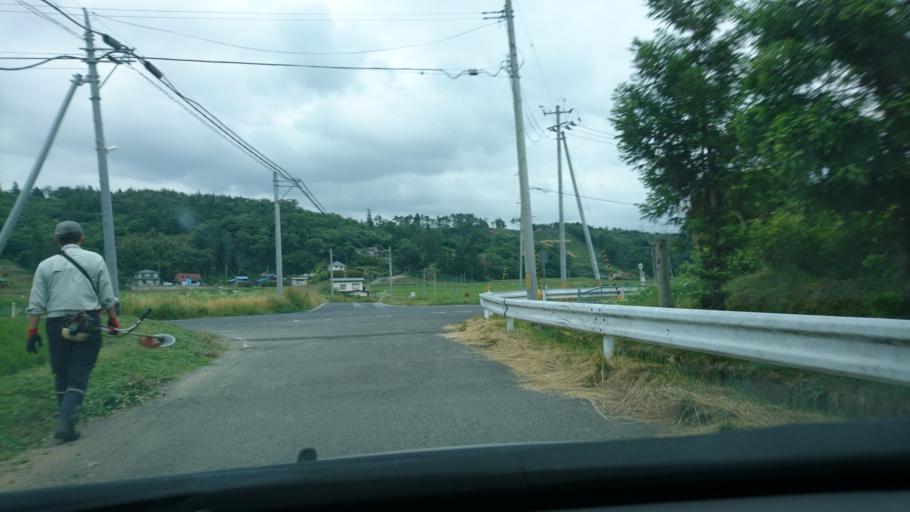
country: JP
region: Iwate
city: Ichinoseki
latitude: 38.9283
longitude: 141.1721
